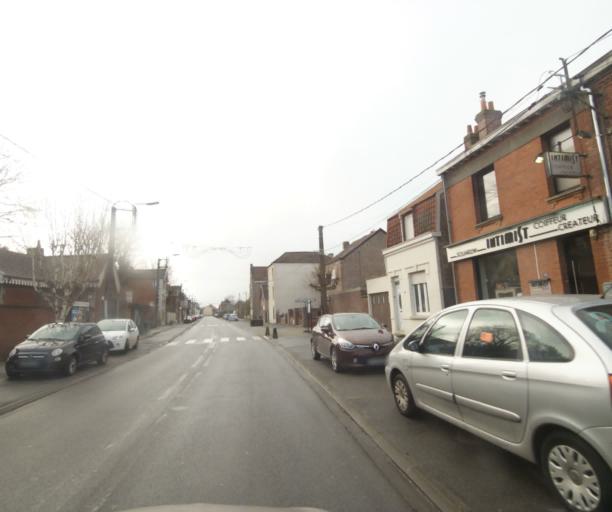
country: FR
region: Nord-Pas-de-Calais
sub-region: Departement du Nord
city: Famars
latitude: 50.3166
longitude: 3.5185
